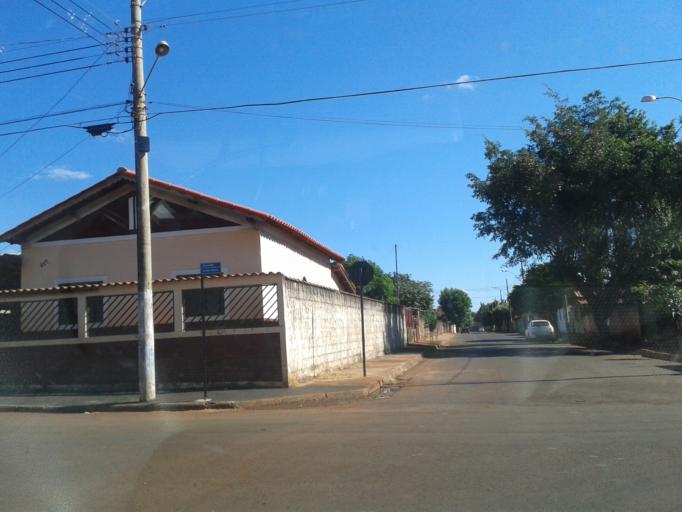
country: BR
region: Minas Gerais
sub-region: Centralina
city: Centralina
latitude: -18.5812
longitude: -49.1996
